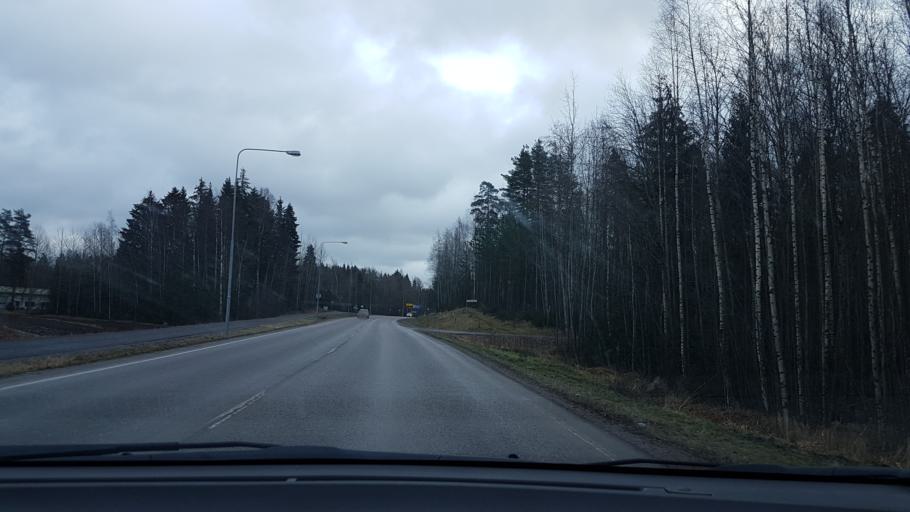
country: FI
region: Uusimaa
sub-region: Helsinki
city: Kerava
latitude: 60.3713
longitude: 25.0664
